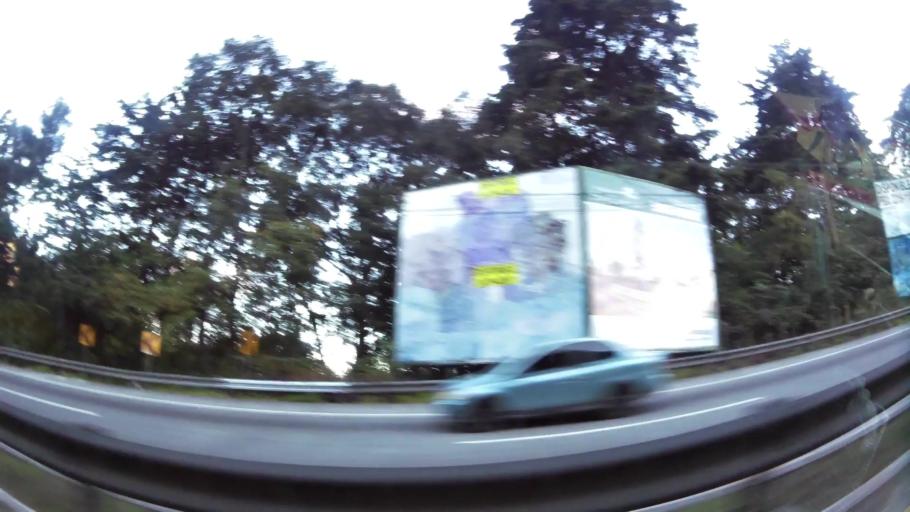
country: GT
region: Guatemala
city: Mixco
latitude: 14.6082
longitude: -90.6237
